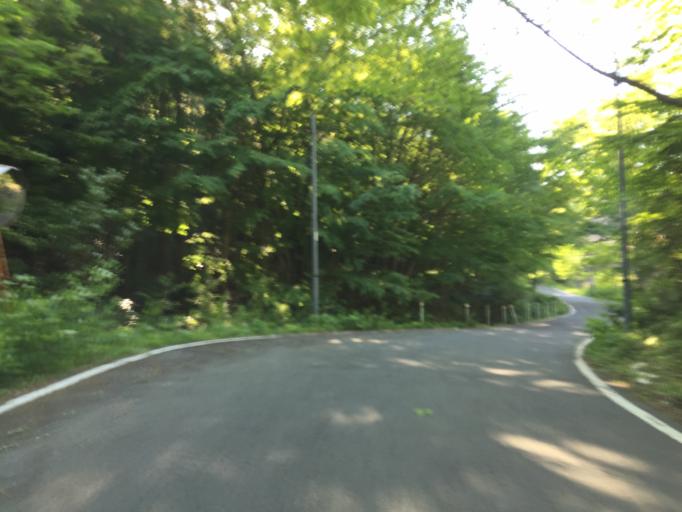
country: JP
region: Ibaraki
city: Kitaibaraki
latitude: 36.8965
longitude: 140.5987
